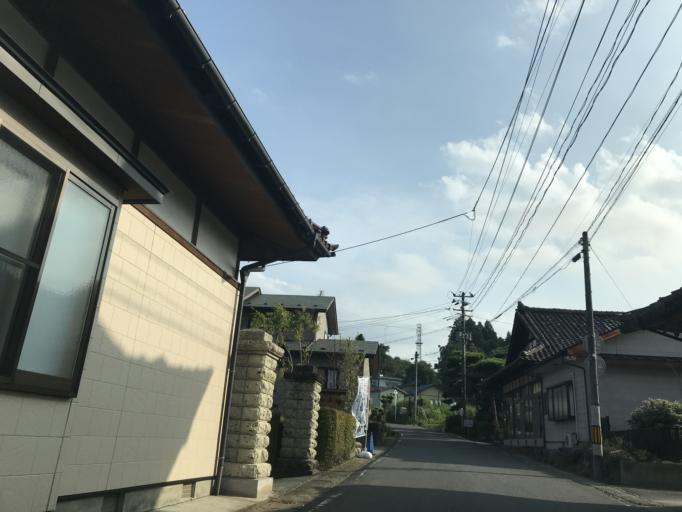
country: JP
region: Iwate
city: Ichinoseki
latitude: 38.8654
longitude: 141.1229
